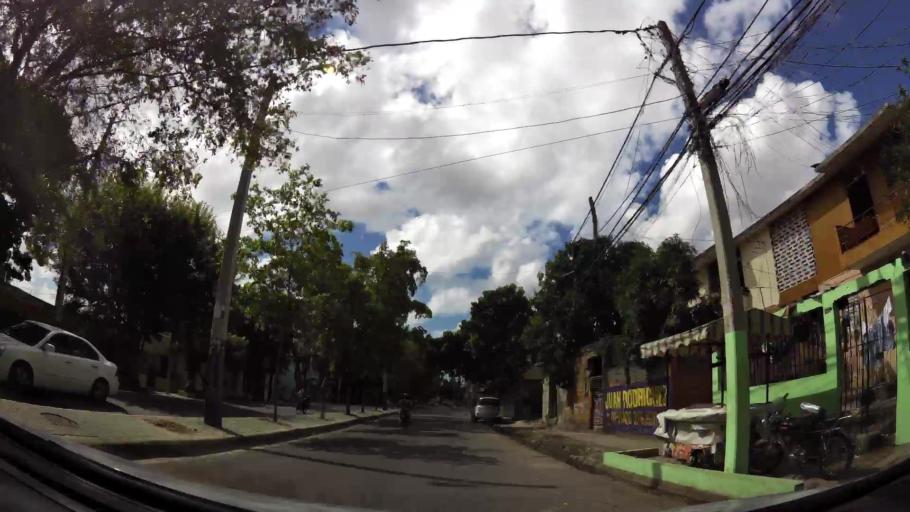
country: DO
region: Nacional
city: Ensanche Luperon
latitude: 18.4923
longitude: -69.8836
